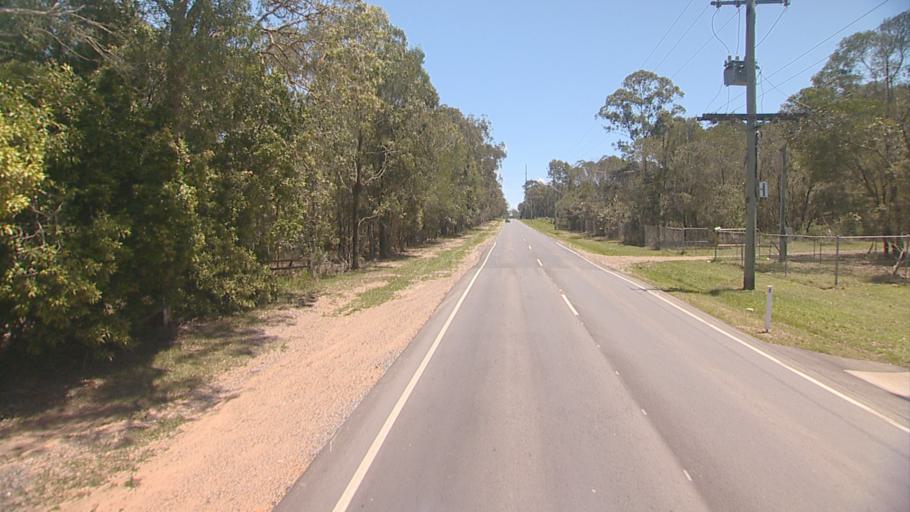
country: AU
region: Queensland
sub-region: Logan
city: Logan Reserve
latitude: -27.7055
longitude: 153.0694
